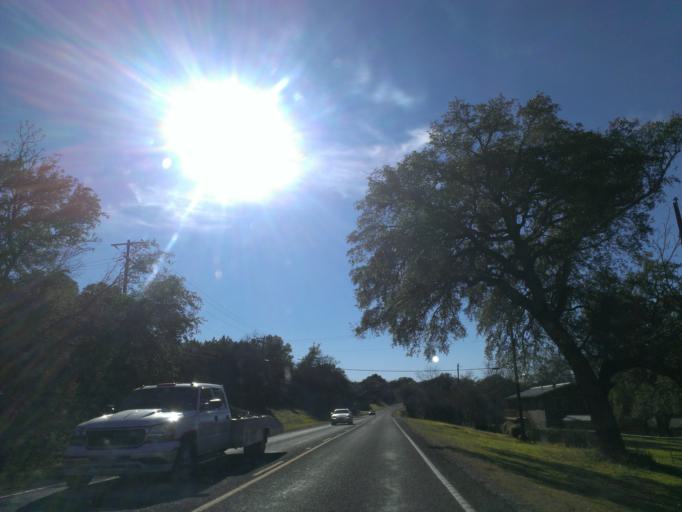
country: US
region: Texas
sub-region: Burnet County
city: Meadowlakes
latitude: 30.5483
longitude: -98.2937
